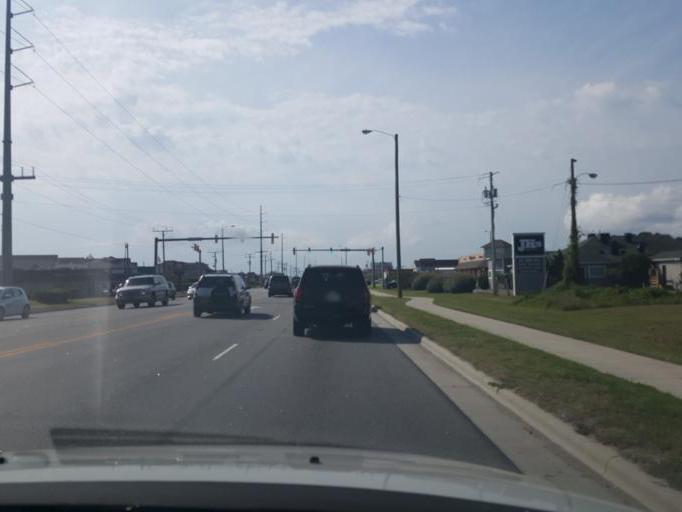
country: US
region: North Carolina
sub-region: Dare County
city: Kill Devil Hills
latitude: 36.0052
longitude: -75.6559
